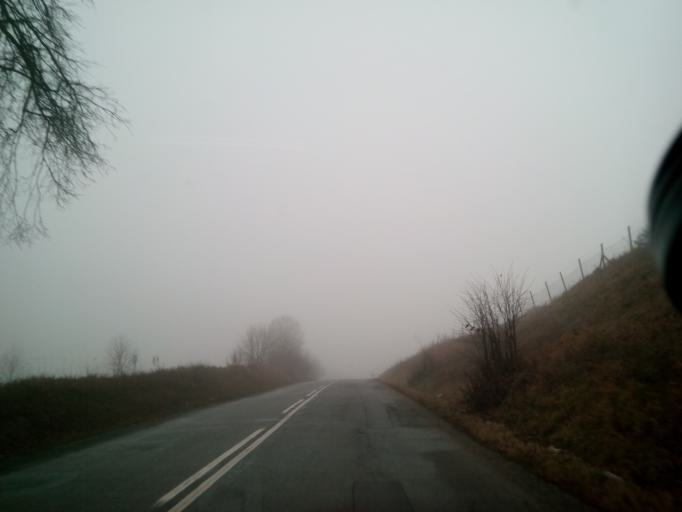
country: SK
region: Presovsky
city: Spisske Podhradie
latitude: 48.9666
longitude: 20.7850
